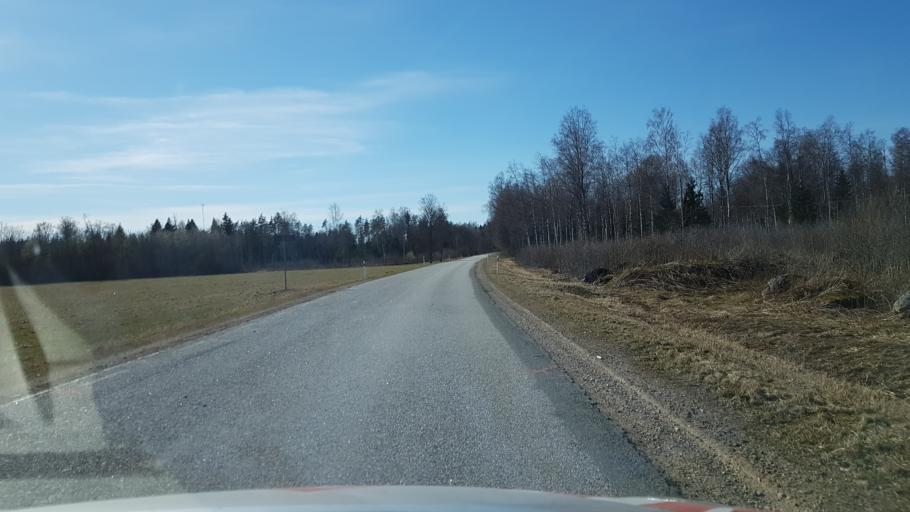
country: EE
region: Ida-Virumaa
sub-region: Aseri vald
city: Aseri
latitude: 59.2296
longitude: 26.7172
